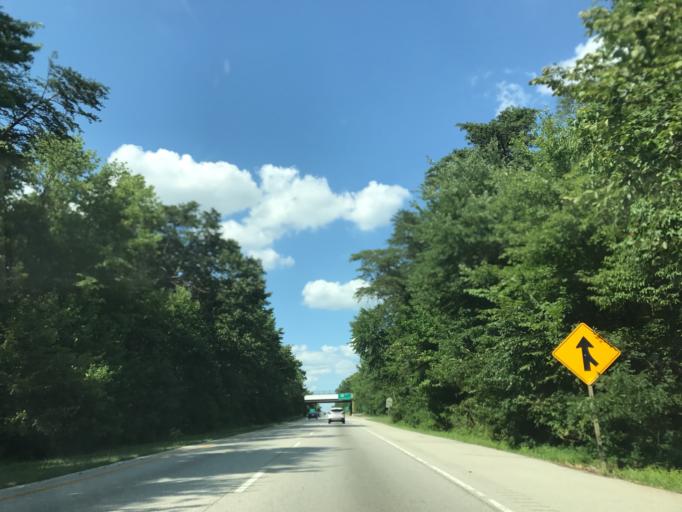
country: US
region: Maryland
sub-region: Anne Arundel County
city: Jessup
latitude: 39.1377
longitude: -76.7565
